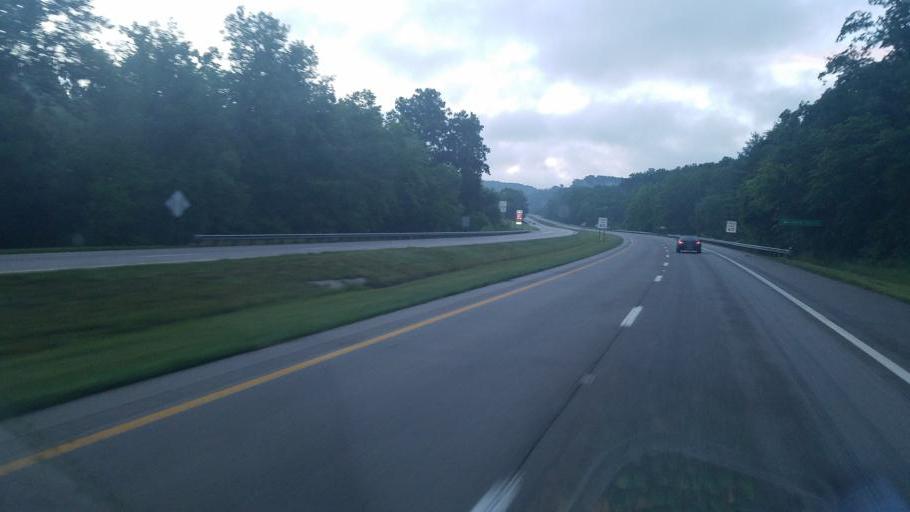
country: US
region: Ohio
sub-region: Pike County
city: Waverly
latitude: 39.1967
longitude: -82.8104
